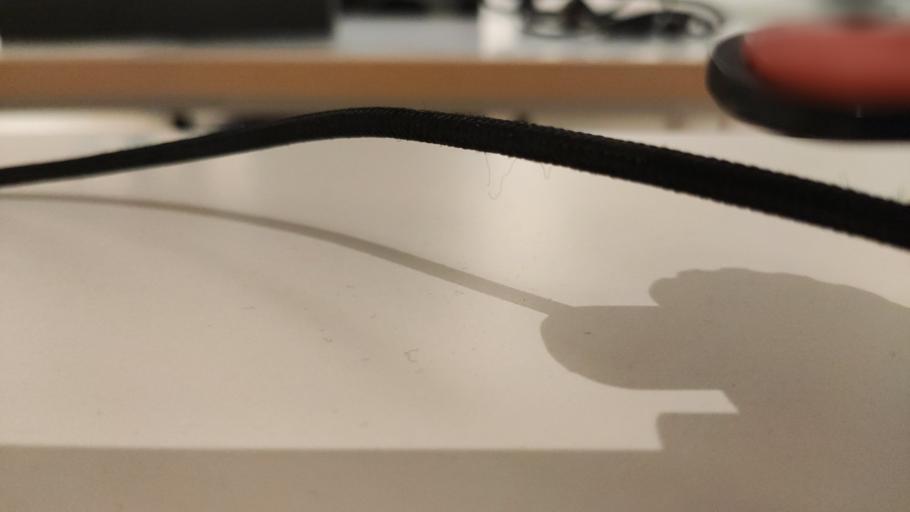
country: RU
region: Moskovskaya
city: Dorokhovo
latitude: 55.3911
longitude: 36.3912
